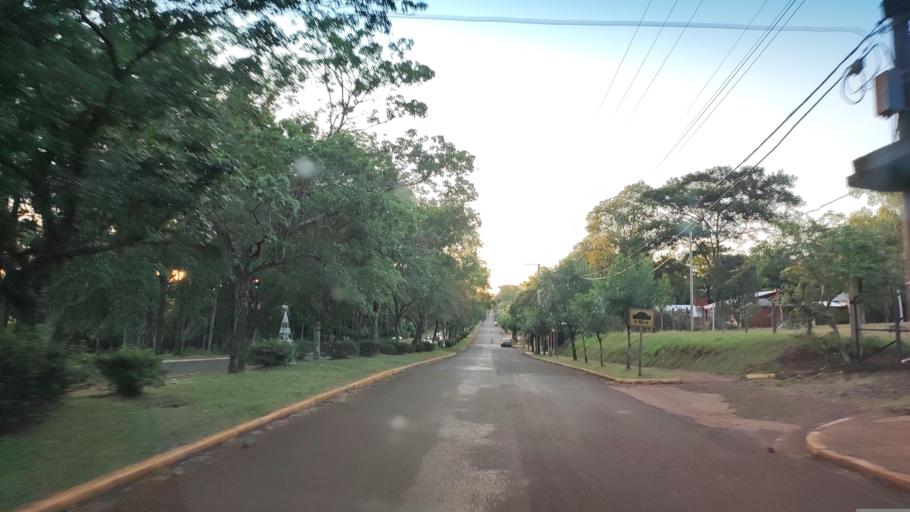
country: AR
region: Misiones
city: Ruiz de Montoya
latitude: -26.9684
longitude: -55.0546
